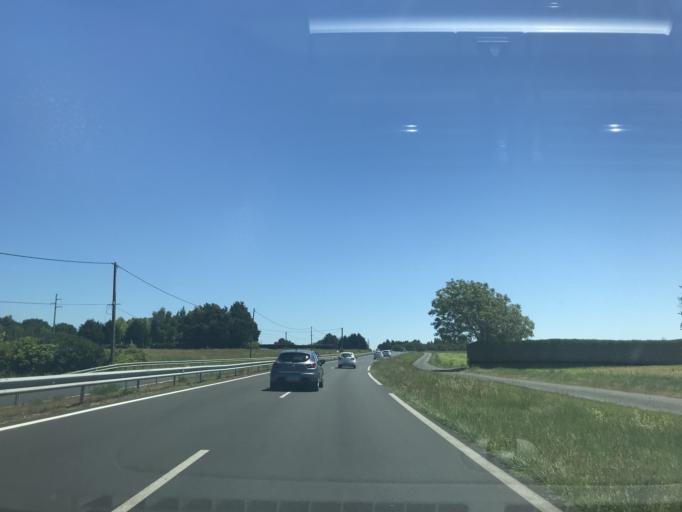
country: FR
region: Poitou-Charentes
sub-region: Departement de la Charente-Maritime
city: Vaux-sur-Mer
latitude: 45.6558
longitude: -1.0549
